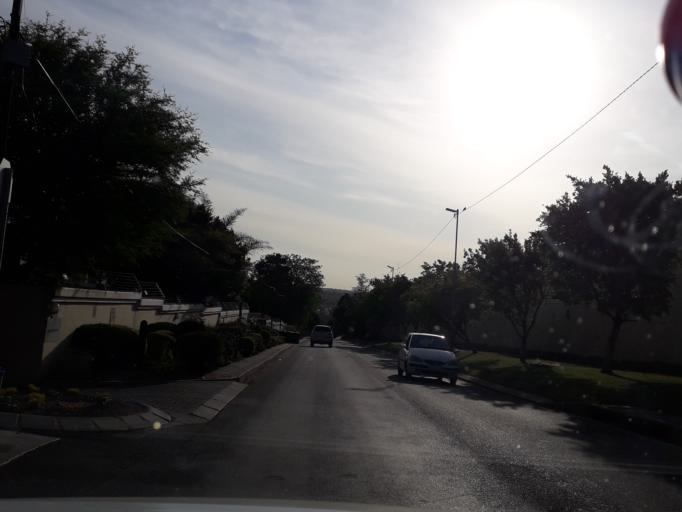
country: ZA
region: Gauteng
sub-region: City of Johannesburg Metropolitan Municipality
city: Diepsloot
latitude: -26.0439
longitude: 27.9952
